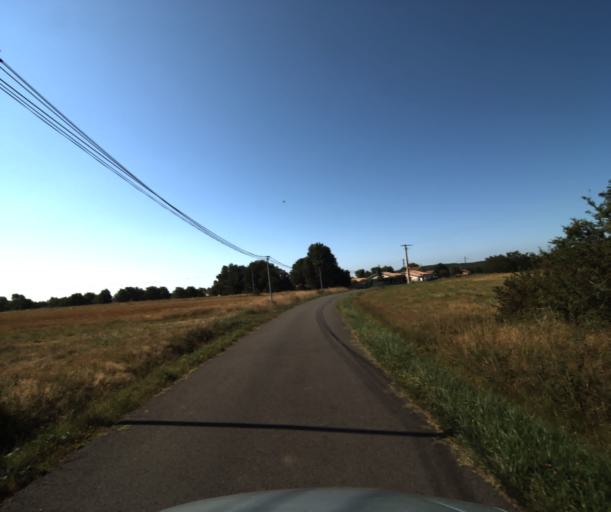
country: FR
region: Midi-Pyrenees
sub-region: Departement de la Haute-Garonne
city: Eaunes
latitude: 43.4329
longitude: 1.3511
